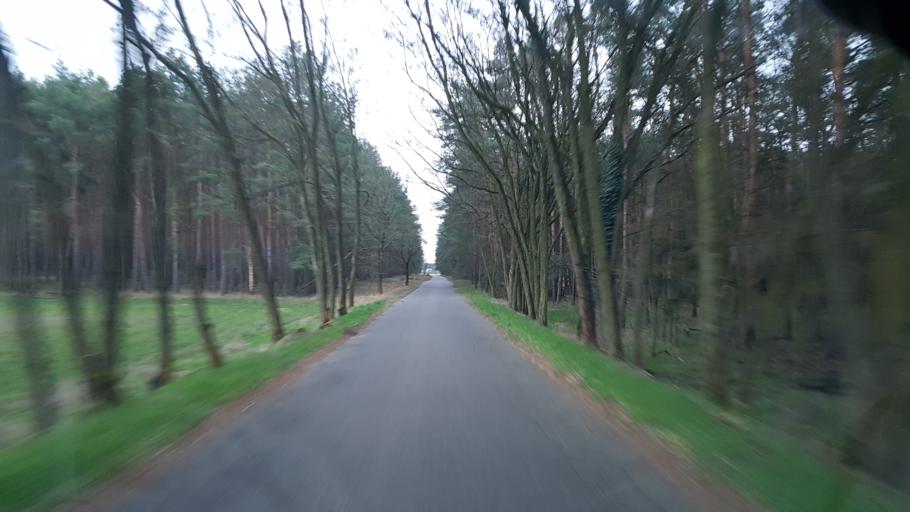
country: DE
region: Brandenburg
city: Schlieben
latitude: 51.7101
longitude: 13.3163
